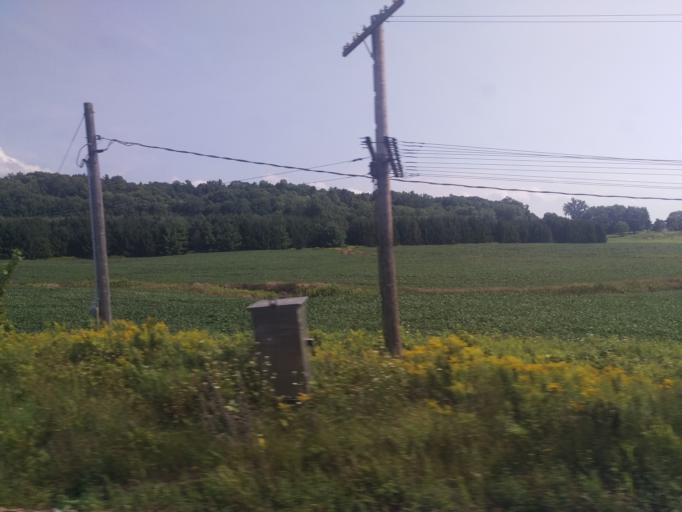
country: CA
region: Ontario
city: Brockville
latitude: 44.5806
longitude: -75.7263
